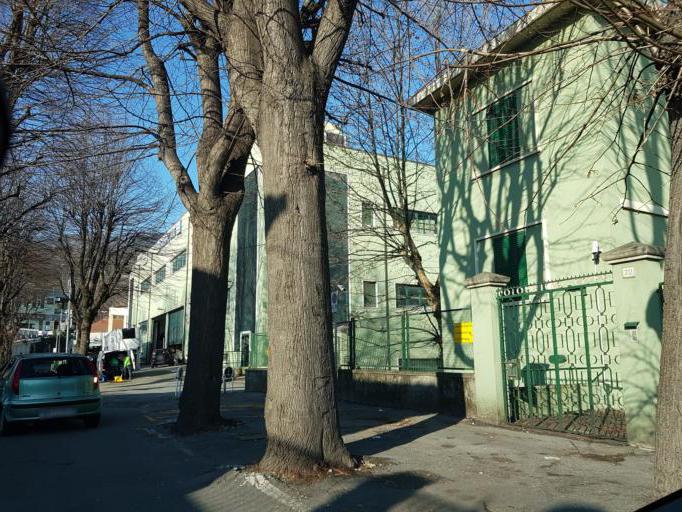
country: IT
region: Liguria
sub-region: Provincia di Genova
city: Santa Marta
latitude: 44.4774
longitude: 8.8994
